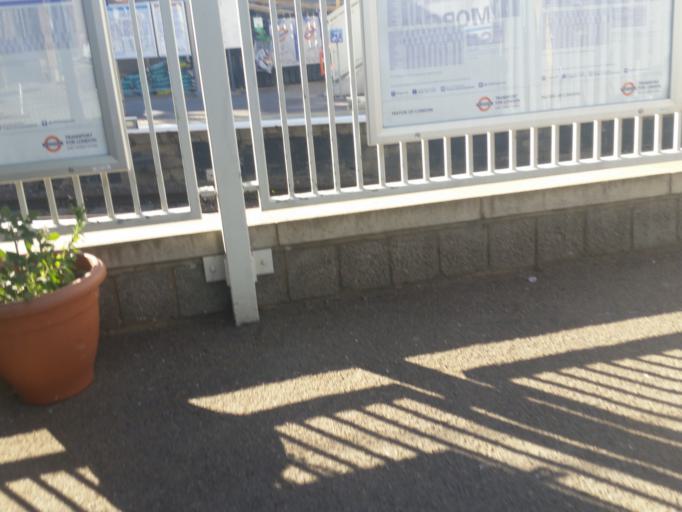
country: GB
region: England
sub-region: Greater London
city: Hammersmith
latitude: 51.5345
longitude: -0.2196
